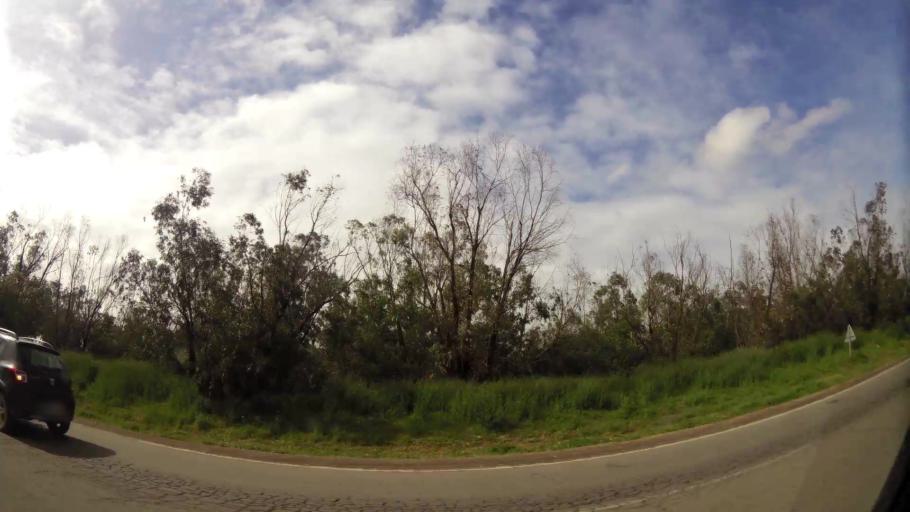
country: MA
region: Grand Casablanca
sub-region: Mohammedia
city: Mohammedia
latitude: 33.6520
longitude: -7.4050
